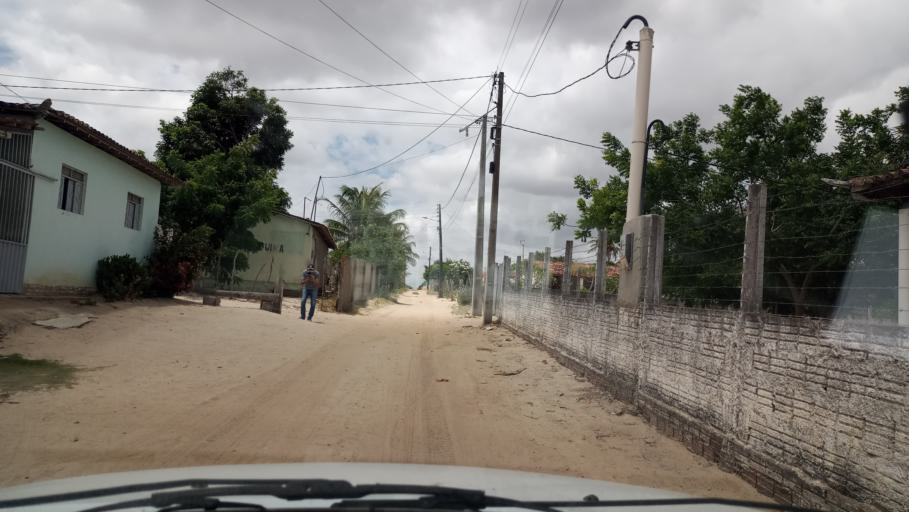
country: BR
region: Rio Grande do Norte
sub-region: Santo Antonio
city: Santo Antonio
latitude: -6.2106
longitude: -35.4676
